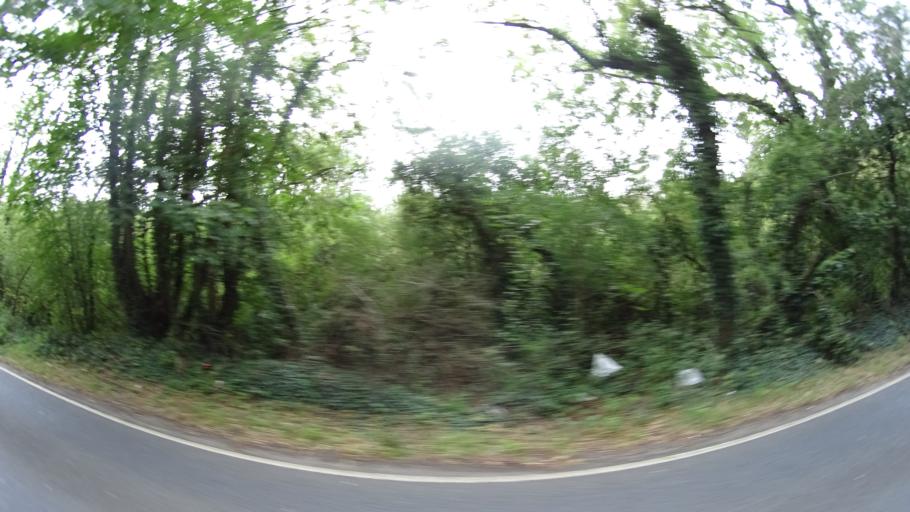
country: GB
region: England
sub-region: Dorset
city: Shaftesbury
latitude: 51.0159
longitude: -2.2167
